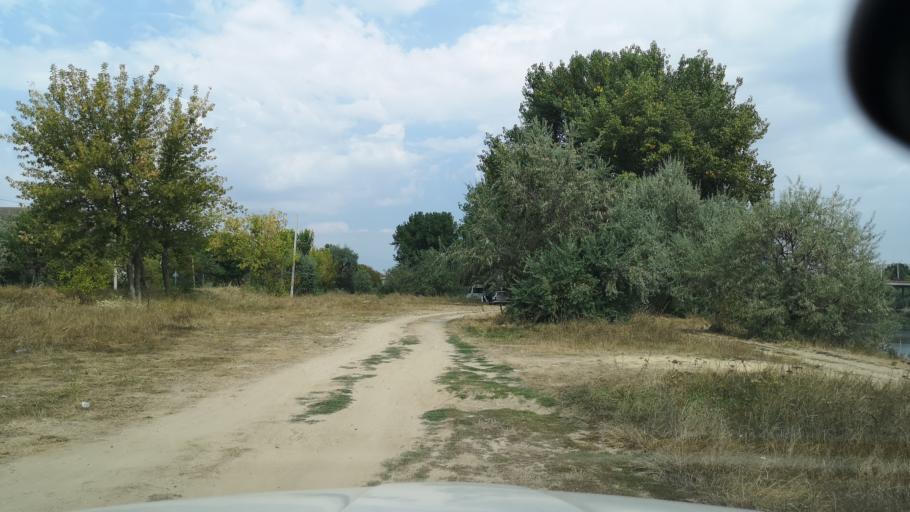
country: MD
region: Rezina
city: Rezina
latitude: 47.7513
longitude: 28.9794
